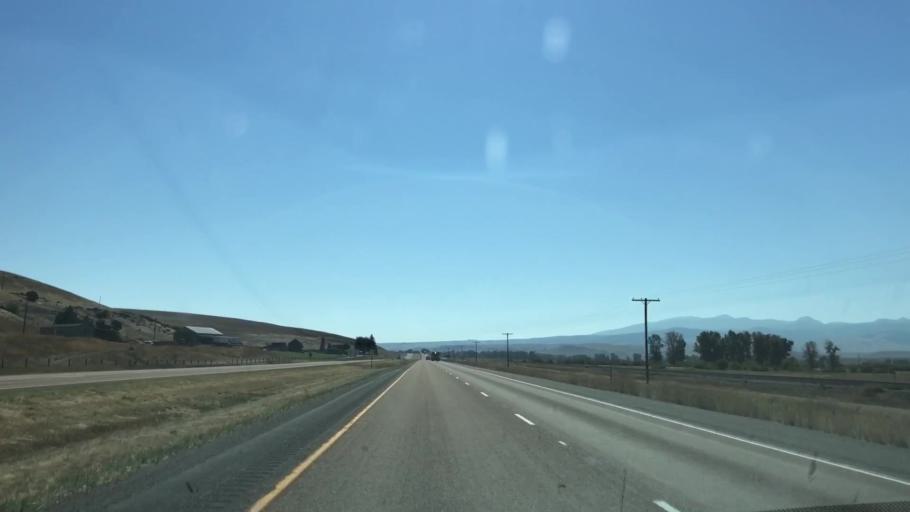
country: US
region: Montana
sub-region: Granite County
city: Philipsburg
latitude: 46.6587
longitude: -113.1314
